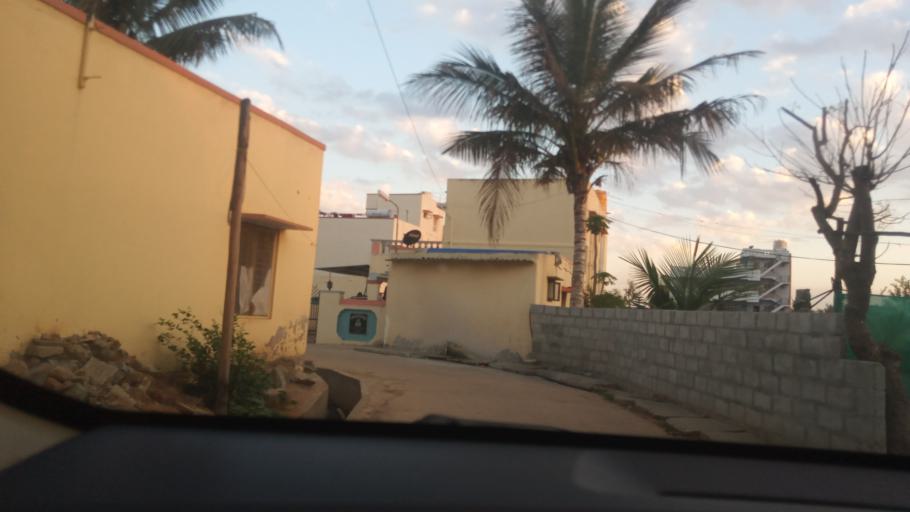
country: IN
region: Karnataka
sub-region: Bangalore Rural
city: Hoskote
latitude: 12.9780
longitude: 77.8011
